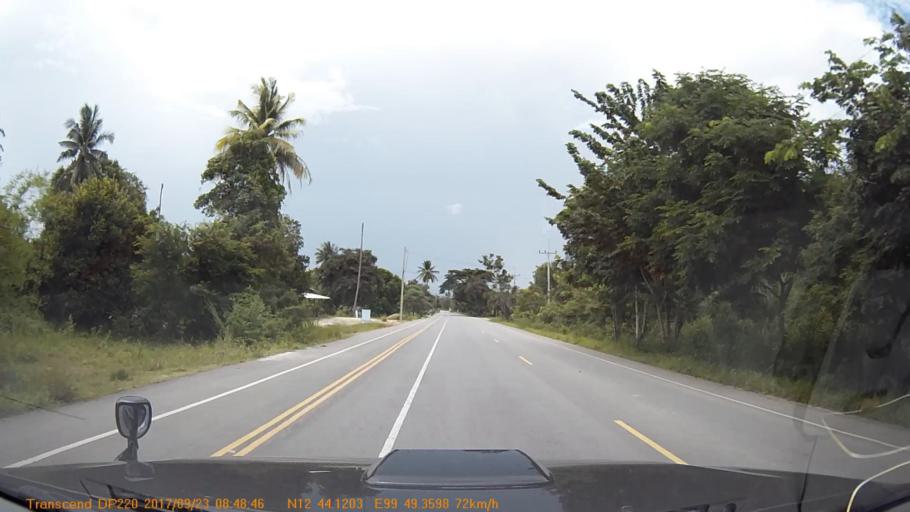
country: TH
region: Phetchaburi
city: Cha-am
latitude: 12.7354
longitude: 99.8226
